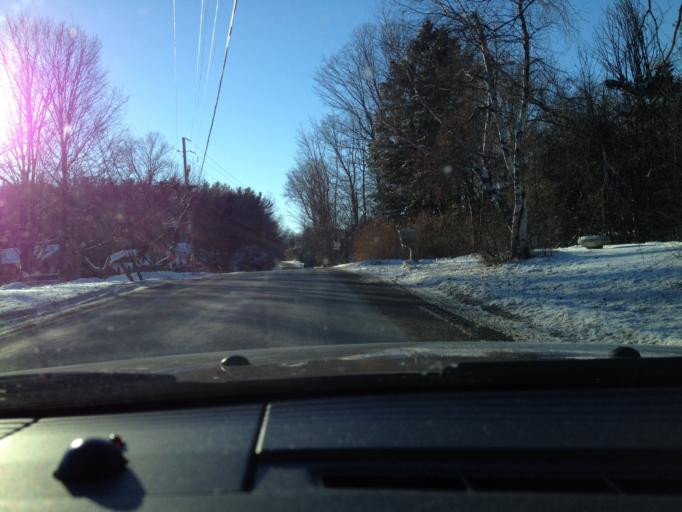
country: US
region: New York
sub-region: Rensselaer County
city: Averill Park
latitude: 42.6236
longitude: -73.5807
